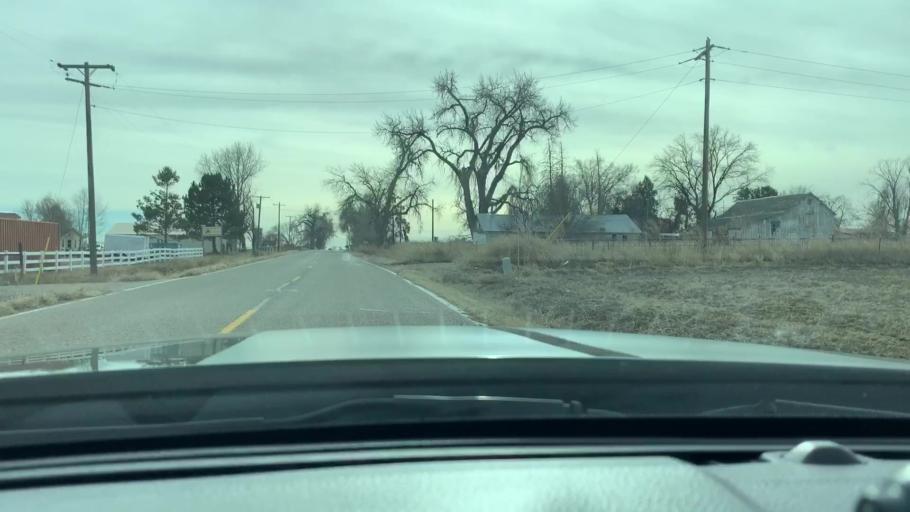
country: US
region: Colorado
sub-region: Weld County
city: Johnstown
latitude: 40.3541
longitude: -104.9835
